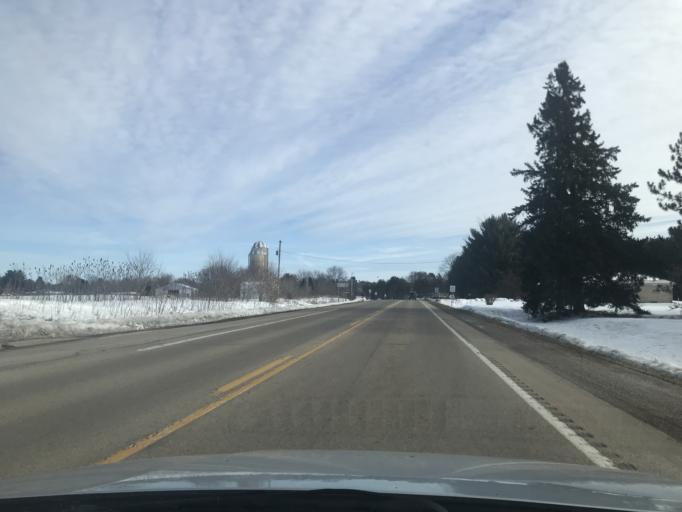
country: US
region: Wisconsin
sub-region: Oconto County
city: Gillett
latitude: 44.8861
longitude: -88.3232
